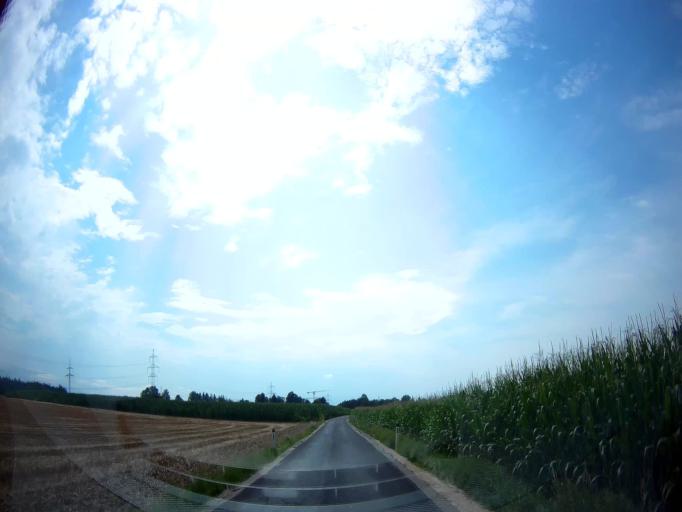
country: AT
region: Upper Austria
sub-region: Wels-Land
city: Sattledt
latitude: 48.0887
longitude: 14.0807
